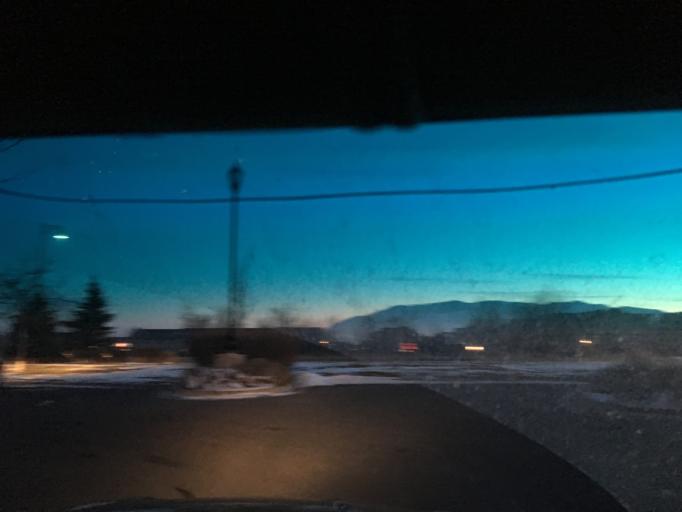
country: US
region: Utah
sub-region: Utah County
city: Saratoga Springs
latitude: 40.3879
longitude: -111.9112
